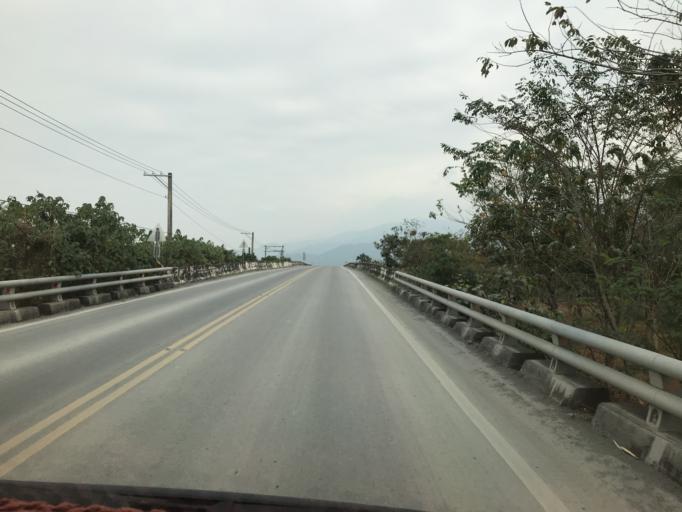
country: TW
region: Taiwan
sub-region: Pingtung
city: Pingtung
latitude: 22.4465
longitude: 120.6053
